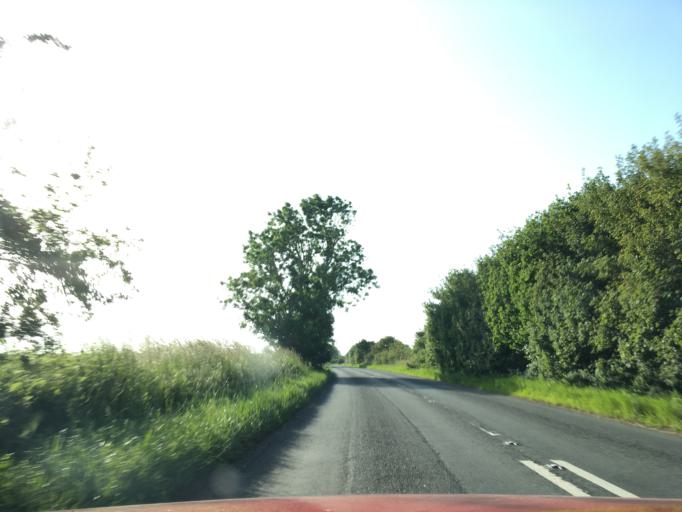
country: GB
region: England
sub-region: Gloucestershire
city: Fairford
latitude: 51.7033
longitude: -1.8422
